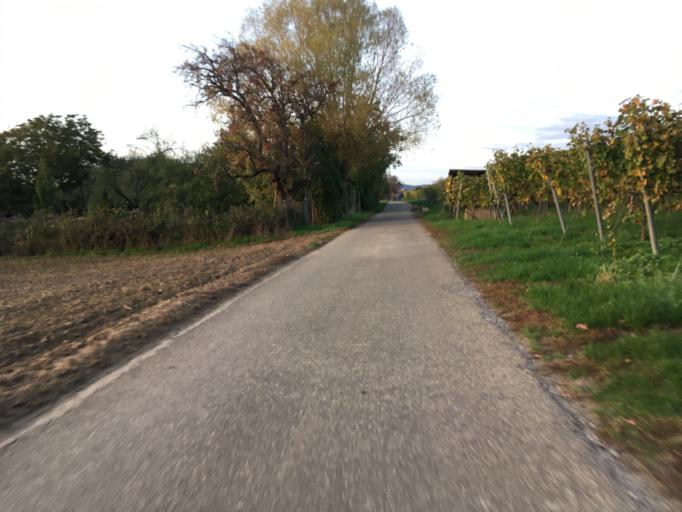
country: DE
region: Baden-Wuerttemberg
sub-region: Karlsruhe Region
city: Leimen
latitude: 49.3642
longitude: 8.6915
